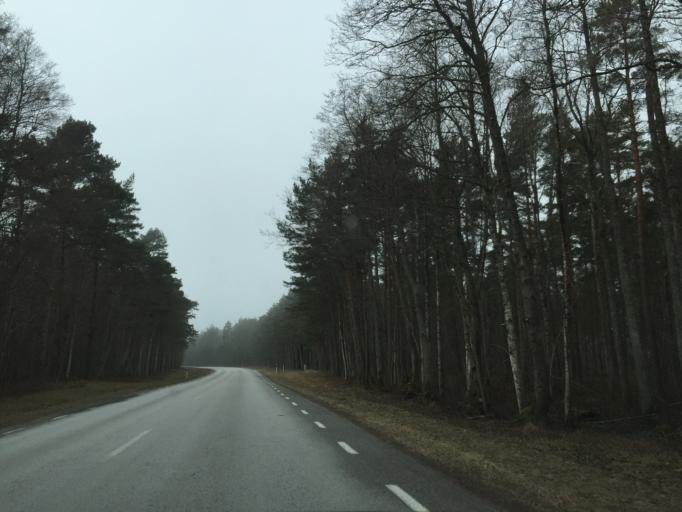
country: EE
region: Saare
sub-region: Kuressaare linn
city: Kuressaare
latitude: 58.2032
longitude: 22.2929
